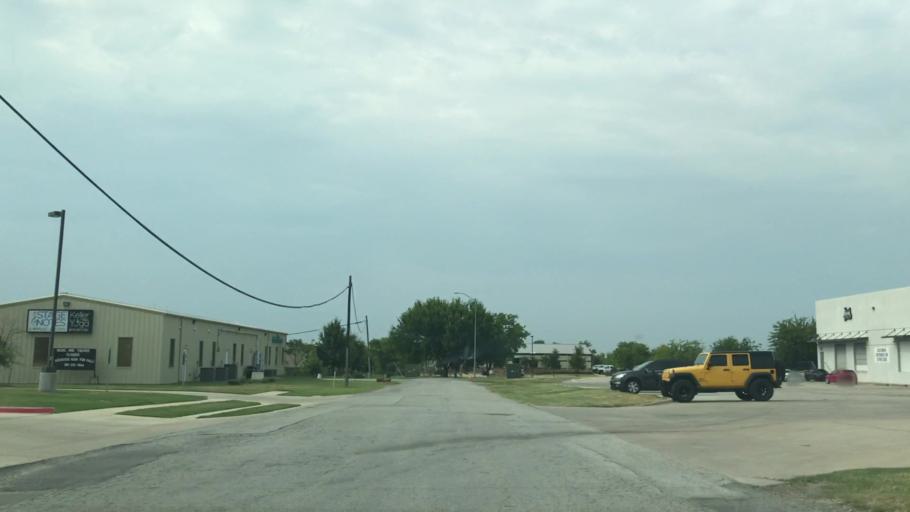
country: US
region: Texas
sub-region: Tarrant County
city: Keller
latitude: 32.9112
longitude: -97.2640
